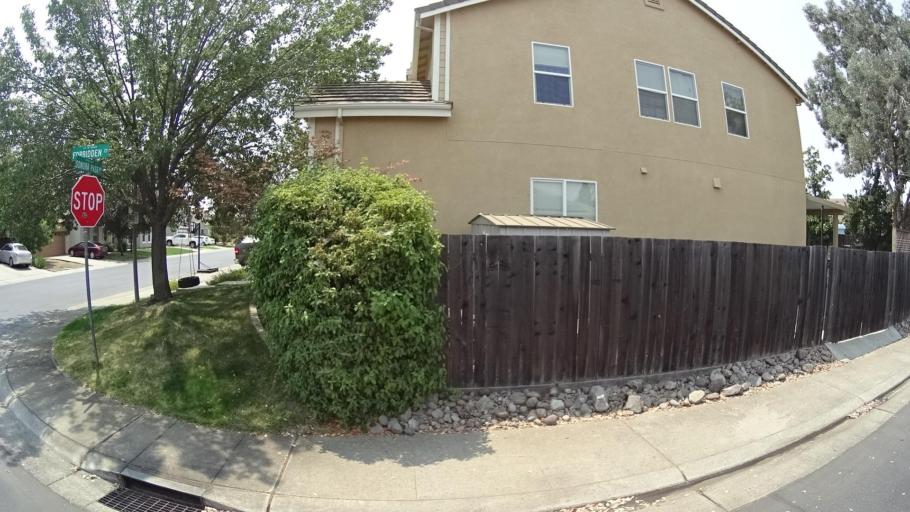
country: US
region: California
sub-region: Placer County
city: Roseville
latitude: 38.7981
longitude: -121.2832
